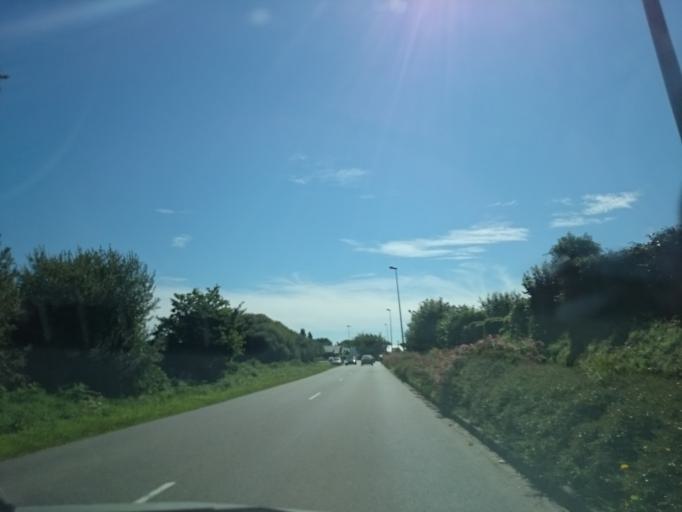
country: FR
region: Brittany
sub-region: Departement du Finistere
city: Saint-Renan
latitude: 48.4369
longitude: -4.6295
